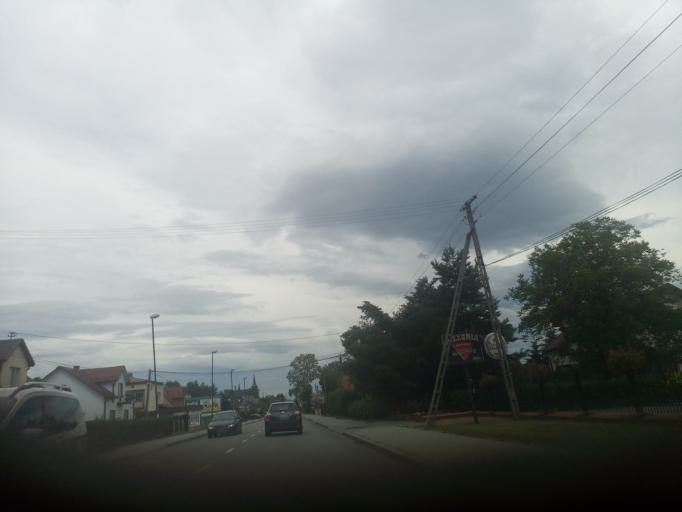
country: PL
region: Lesser Poland Voivodeship
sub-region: Powiat nowosadecki
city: Nawojowa
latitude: 49.5757
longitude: 20.7322
